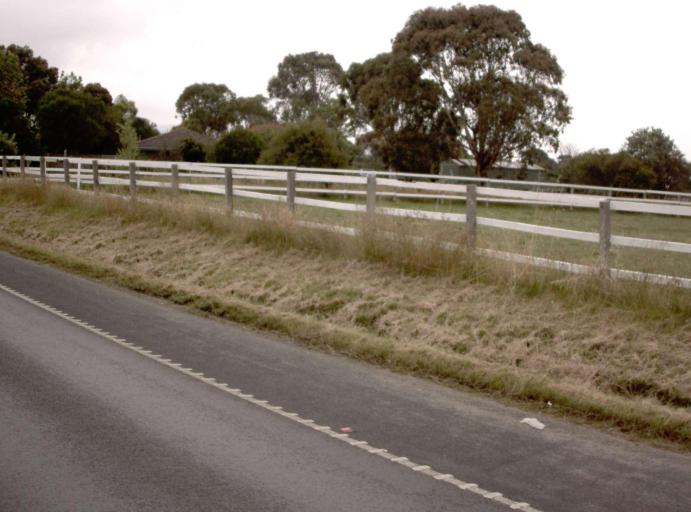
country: AU
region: Victoria
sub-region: Latrobe
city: Morwell
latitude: -38.2973
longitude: 146.4174
